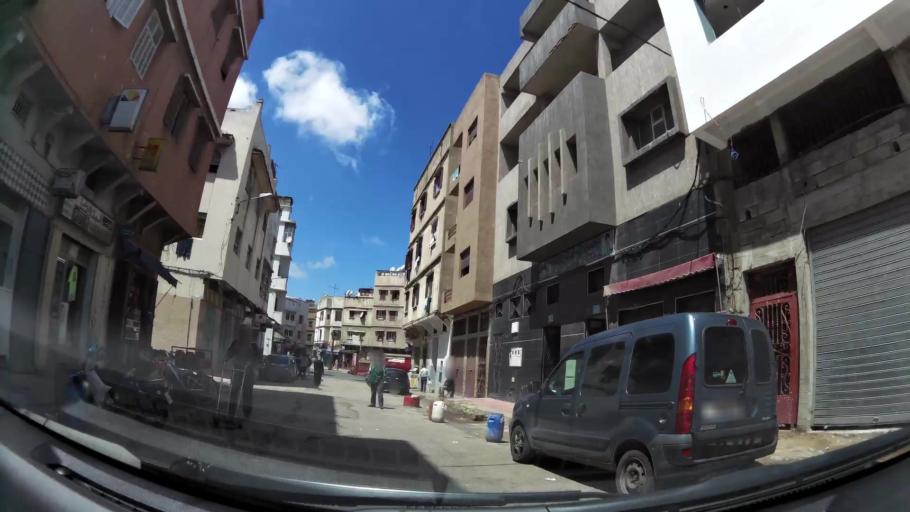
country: MA
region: Grand Casablanca
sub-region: Casablanca
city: Casablanca
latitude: 33.5667
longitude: -7.6060
